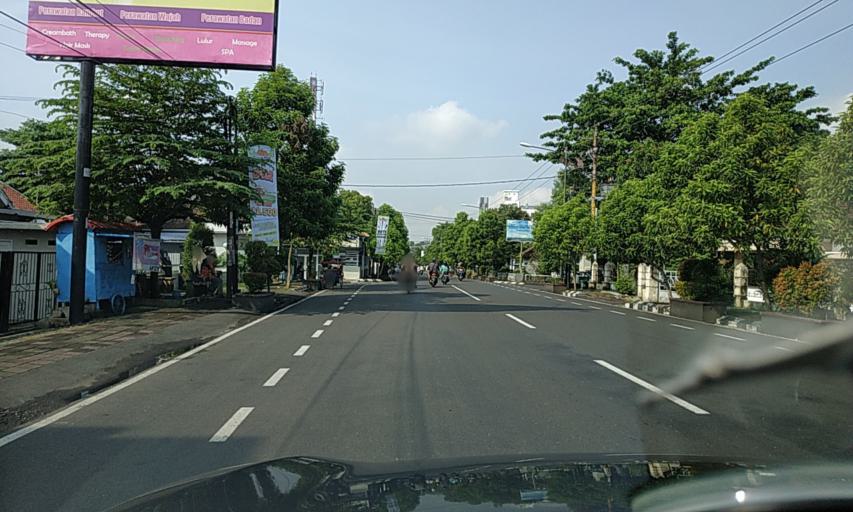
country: ID
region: Central Java
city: Purwokerto
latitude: -7.4232
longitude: 109.2375
